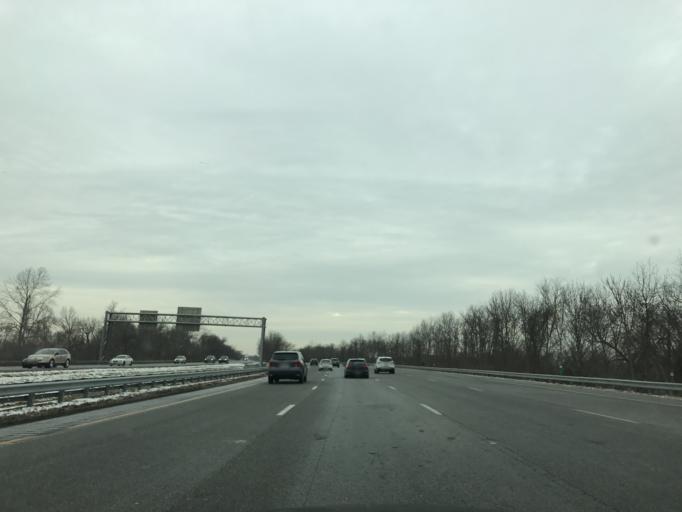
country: US
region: New Jersey
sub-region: Burlington County
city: Bordentown
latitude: 40.1570
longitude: -74.7178
